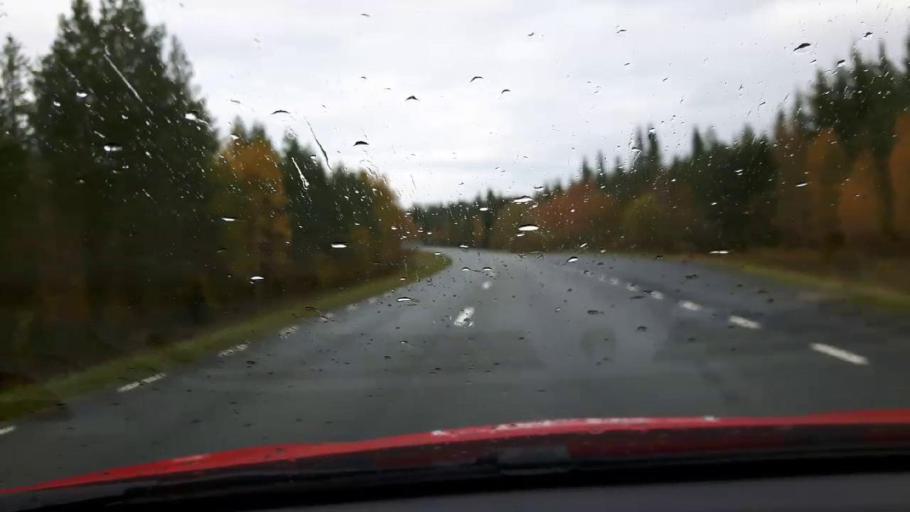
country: SE
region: Jaemtland
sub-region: Krokoms Kommun
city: Krokom
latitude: 63.0926
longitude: 14.3018
